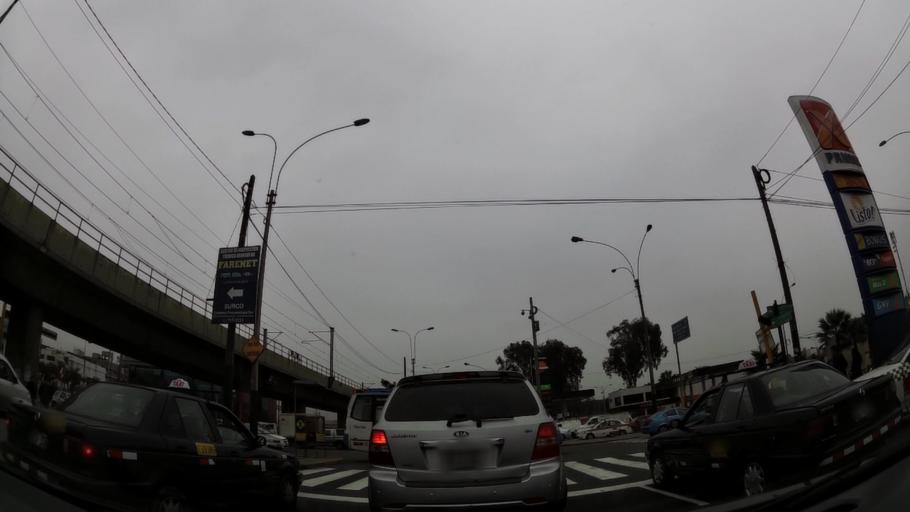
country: PE
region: Lima
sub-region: Lima
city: Surco
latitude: -12.1478
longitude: -76.9864
